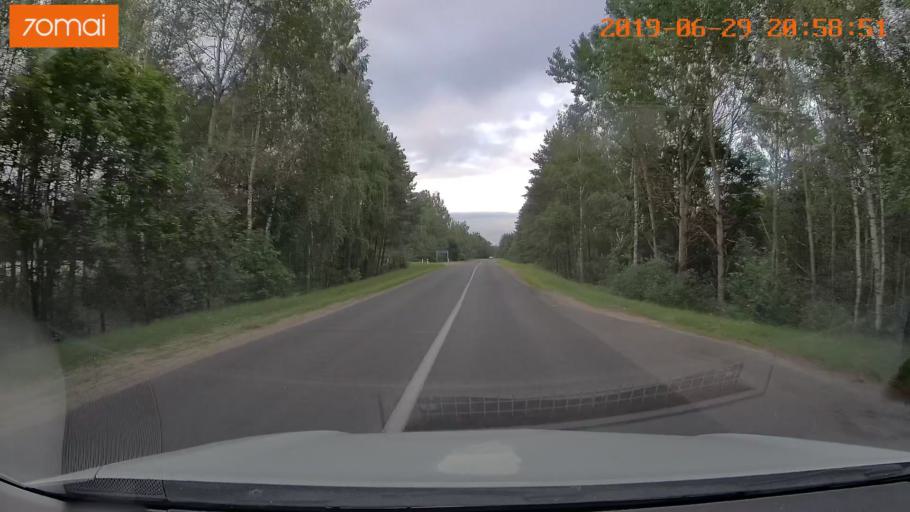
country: BY
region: Brest
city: Hantsavichy
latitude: 52.7333
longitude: 26.3943
